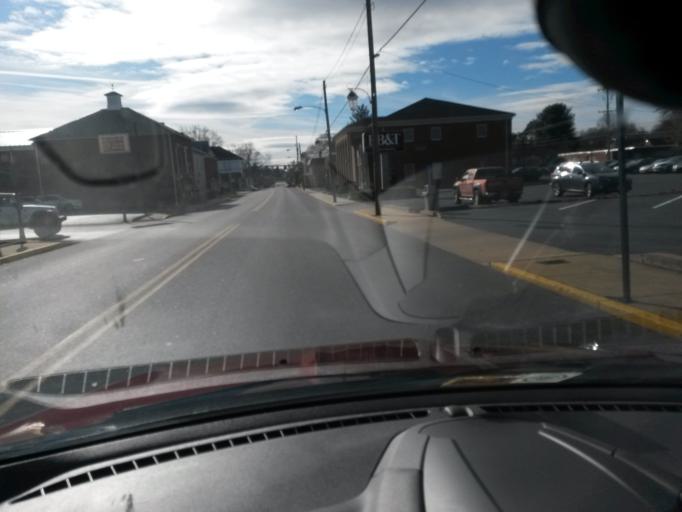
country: US
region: Virginia
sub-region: Rockingham County
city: Bridgewater
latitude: 38.3832
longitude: -78.9757
